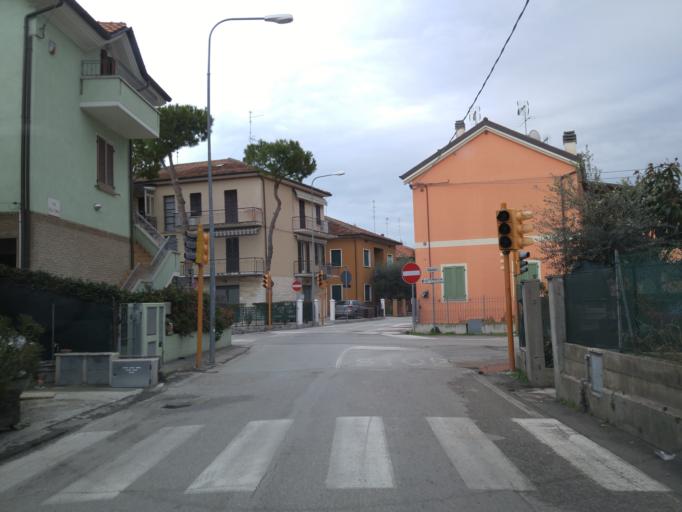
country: IT
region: The Marches
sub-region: Provincia di Pesaro e Urbino
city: Centinarola
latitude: 43.8369
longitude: 13.0026
